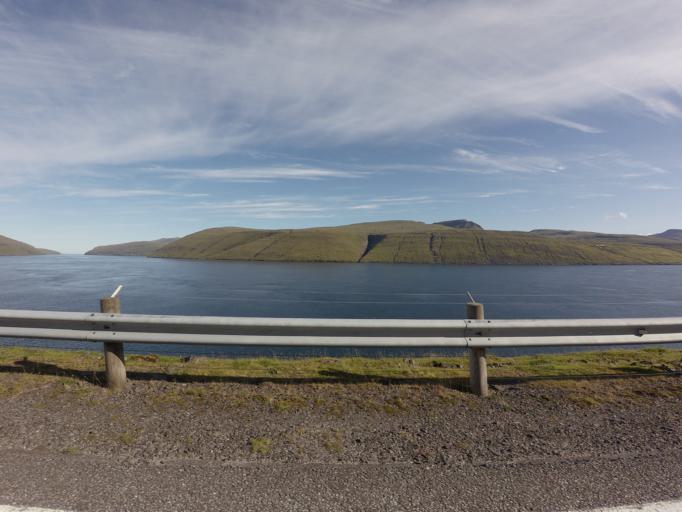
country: FO
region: Streymoy
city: Vestmanna
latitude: 62.1005
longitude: -7.1276
